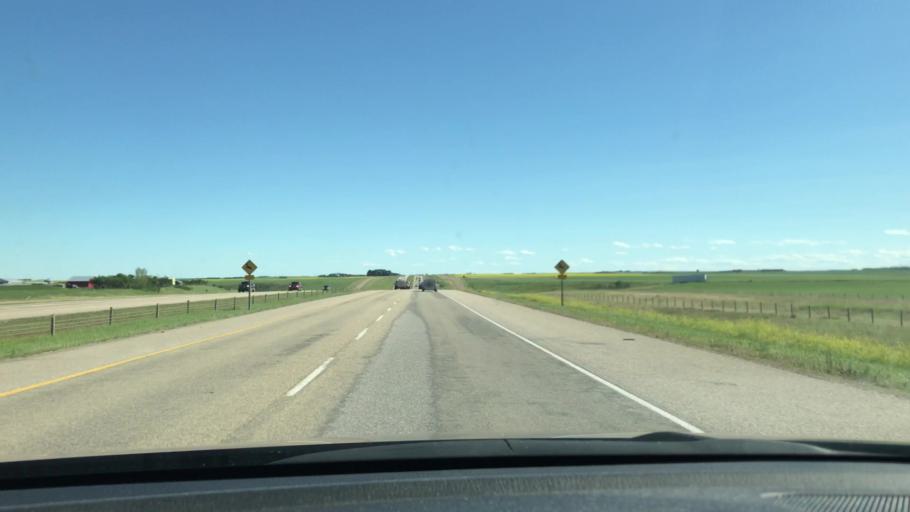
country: CA
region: Alberta
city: Carstairs
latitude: 51.6051
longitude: -114.0256
